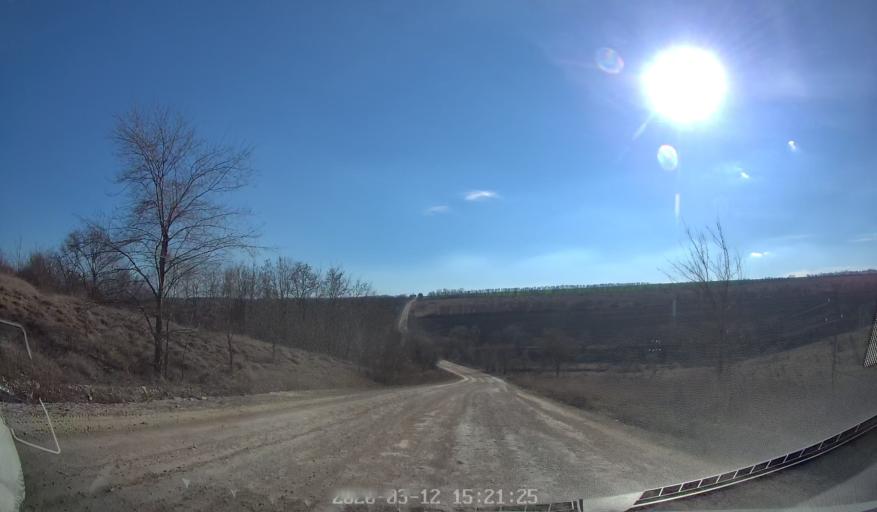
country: MD
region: Chisinau
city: Ciorescu
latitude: 47.2028
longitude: 28.9226
